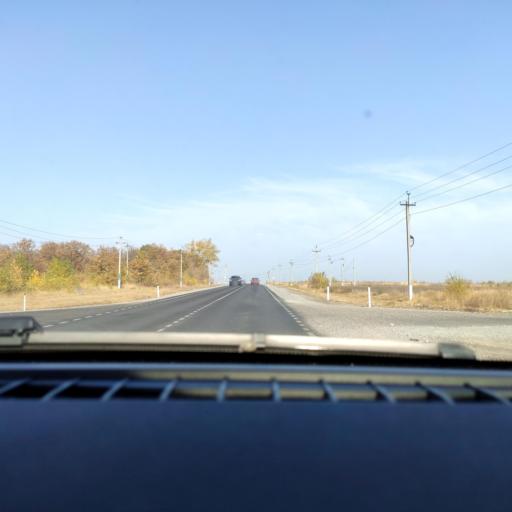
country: RU
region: Voronezj
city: Novaya Usman'
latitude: 51.6845
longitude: 39.3968
